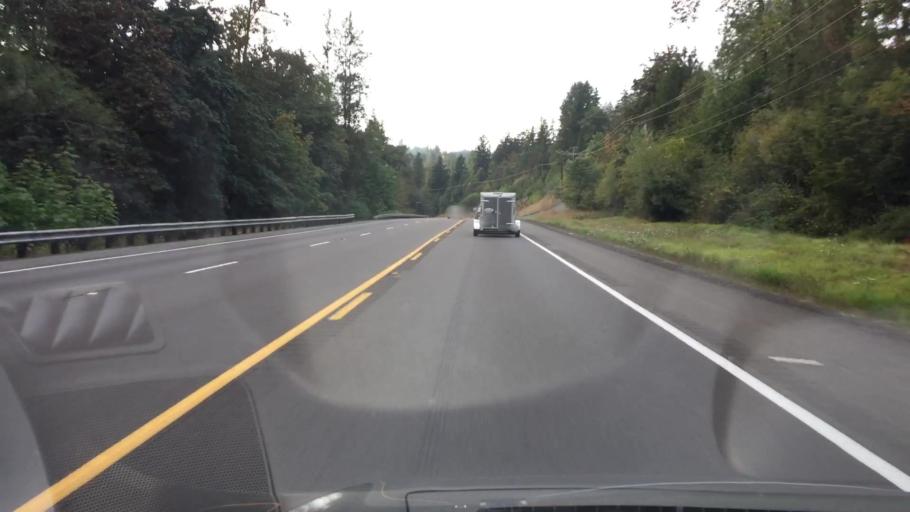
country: US
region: Washington
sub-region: Lewis County
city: Napavine
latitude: 46.5310
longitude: -122.6087
